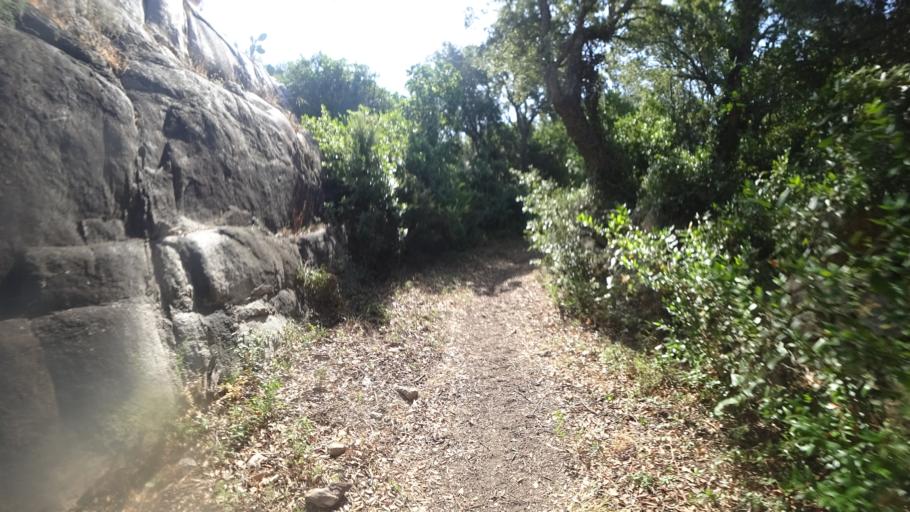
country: FR
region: Corsica
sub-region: Departement de la Corse-du-Sud
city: Porto-Vecchio
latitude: 41.6642
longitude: 9.3268
